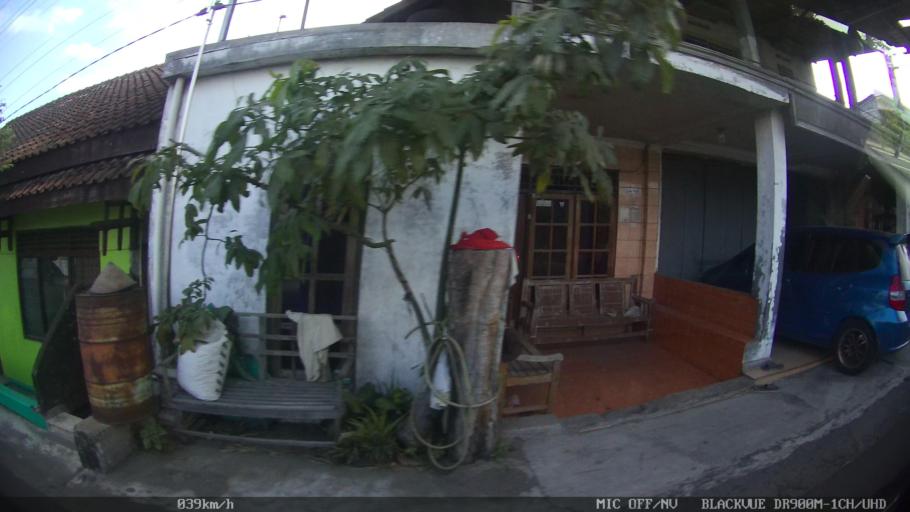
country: ID
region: Central Java
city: Candi Prambanan
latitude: -7.6984
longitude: 110.4651
